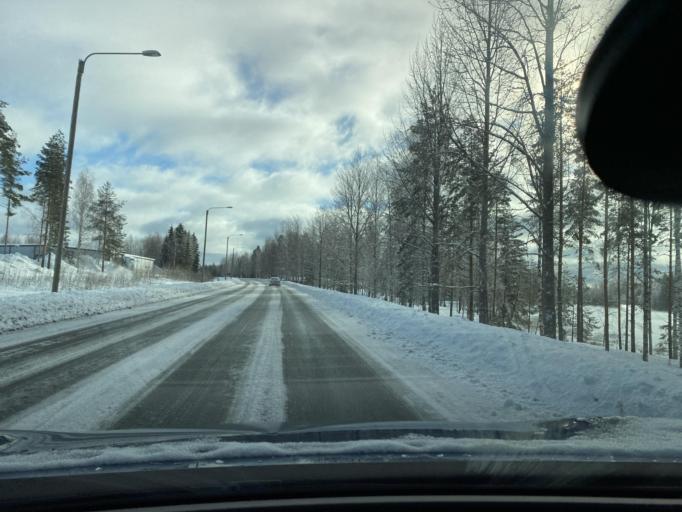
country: FI
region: Southern Savonia
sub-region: Mikkeli
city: Kangasniemi
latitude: 62.0076
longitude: 26.6418
